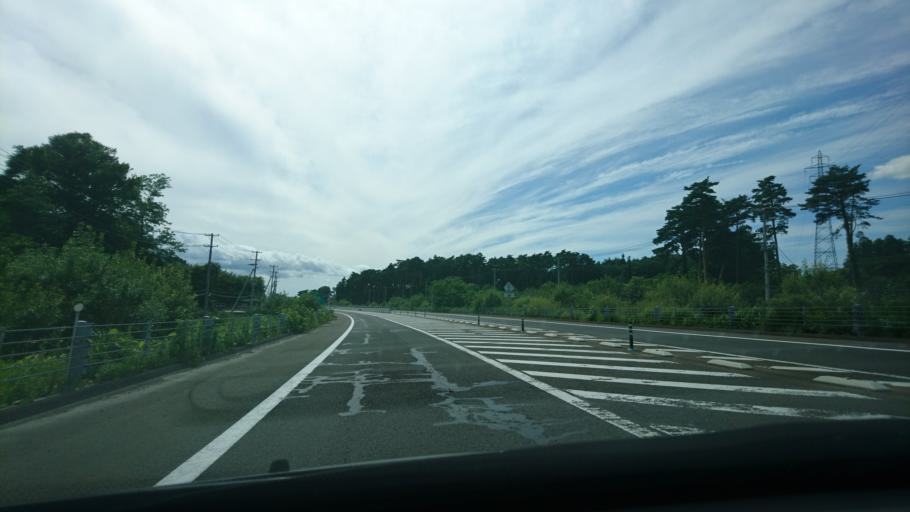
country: JP
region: Aomori
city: Hachinohe
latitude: 40.4844
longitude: 141.5677
